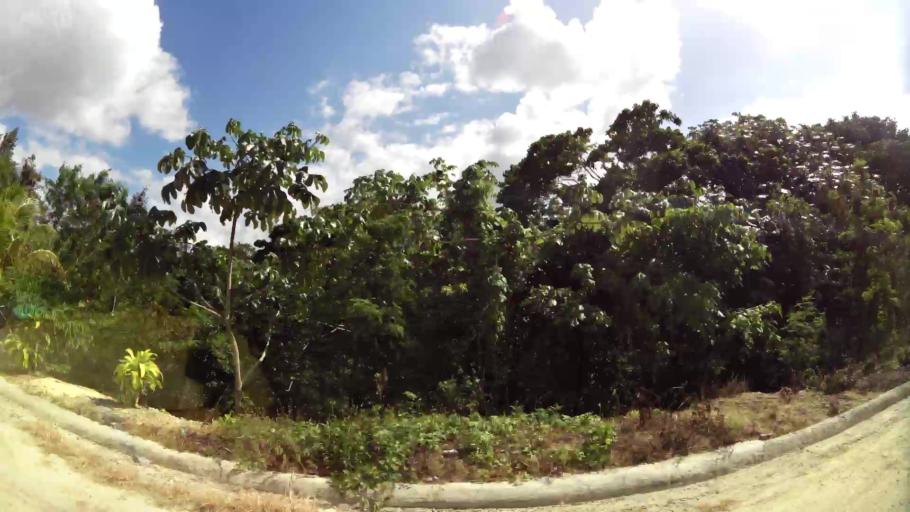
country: DO
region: Nacional
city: Ensanche Luperon
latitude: 18.5288
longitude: -69.8975
